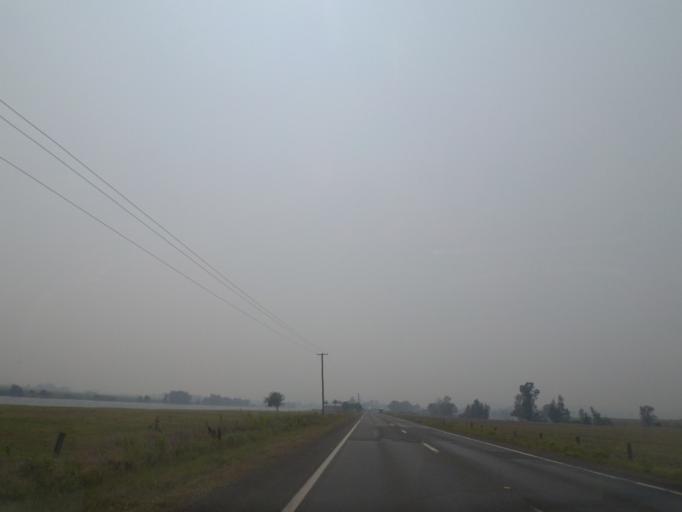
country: AU
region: New South Wales
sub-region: Clarence Valley
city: Maclean
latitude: -29.5653
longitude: 153.1190
